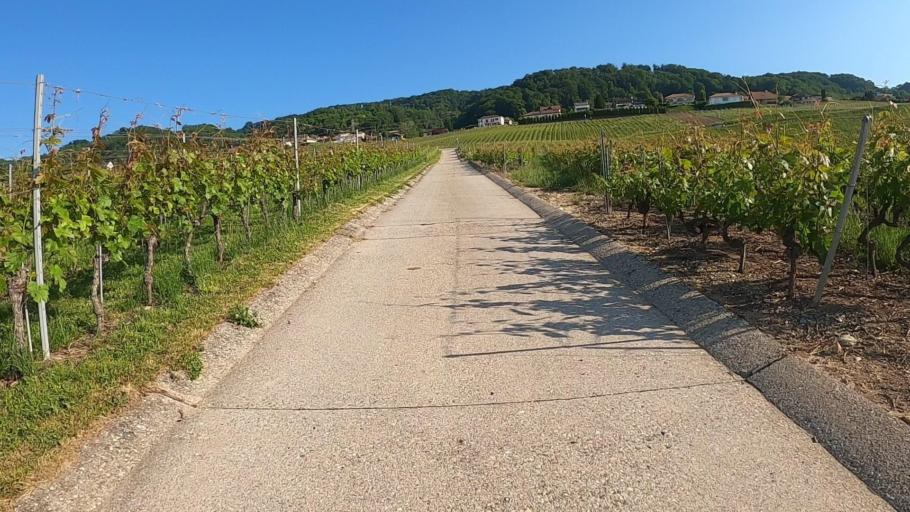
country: CH
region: Vaud
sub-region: Nyon District
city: Rolle
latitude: 46.4722
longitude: 6.3375
